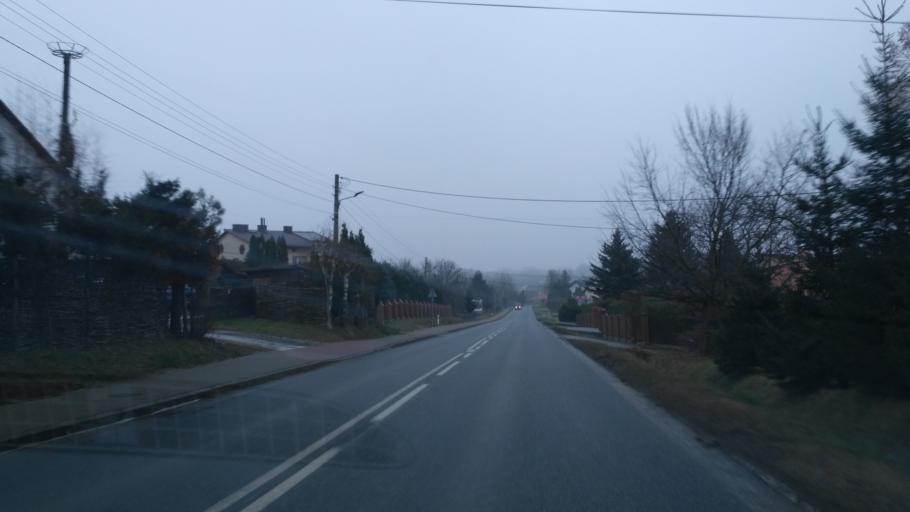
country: PL
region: Subcarpathian Voivodeship
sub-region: Powiat lancucki
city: Sonina
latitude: 50.0584
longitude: 22.2630
